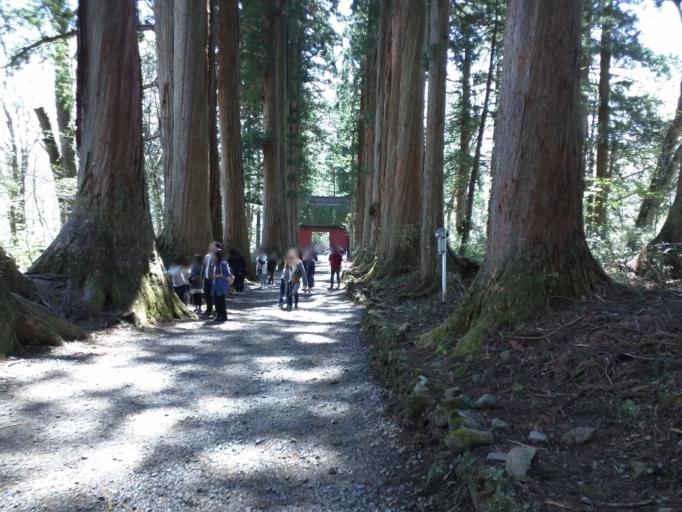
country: JP
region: Nagano
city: Nagano-shi
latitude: 36.7615
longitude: 138.0679
